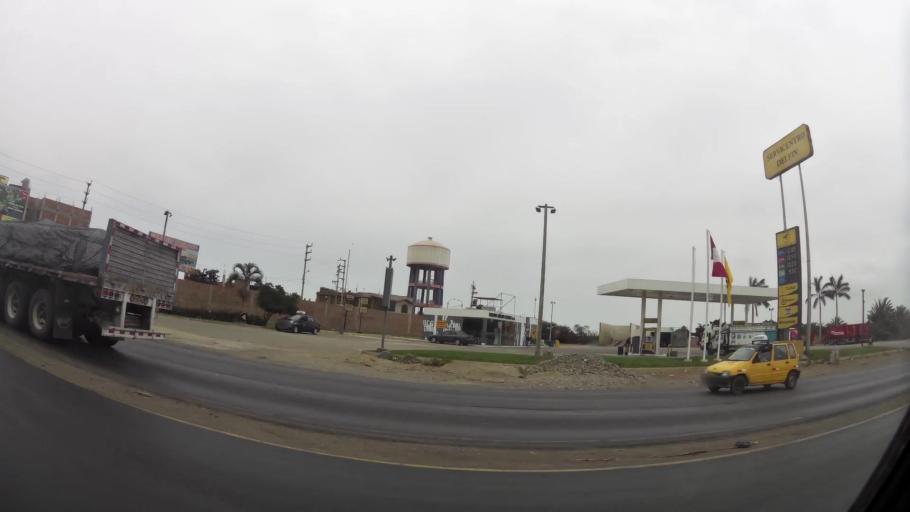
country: PE
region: La Libertad
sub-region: Provincia de Trujillo
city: Moche
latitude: -8.1503
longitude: -79.0113
